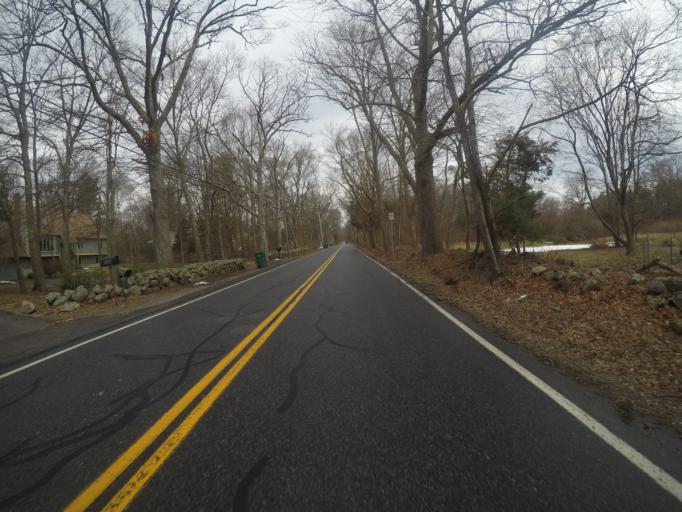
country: US
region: Massachusetts
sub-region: Bristol County
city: Easton
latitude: 42.0576
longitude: -71.1660
